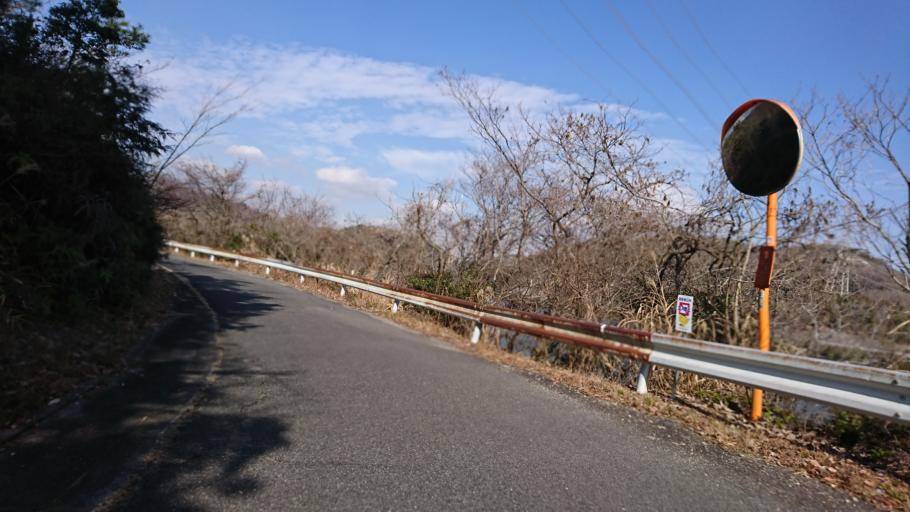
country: JP
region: Hyogo
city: Ono
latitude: 34.8274
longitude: 134.8738
